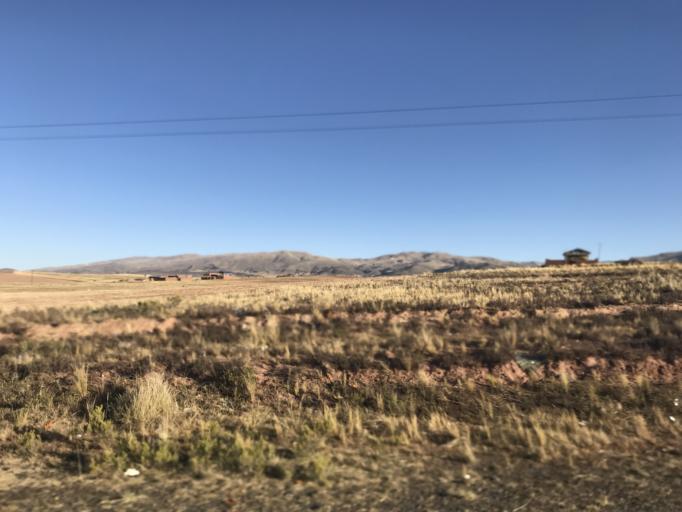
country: BO
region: La Paz
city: Tiahuanaco
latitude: -16.5634
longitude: -68.6289
